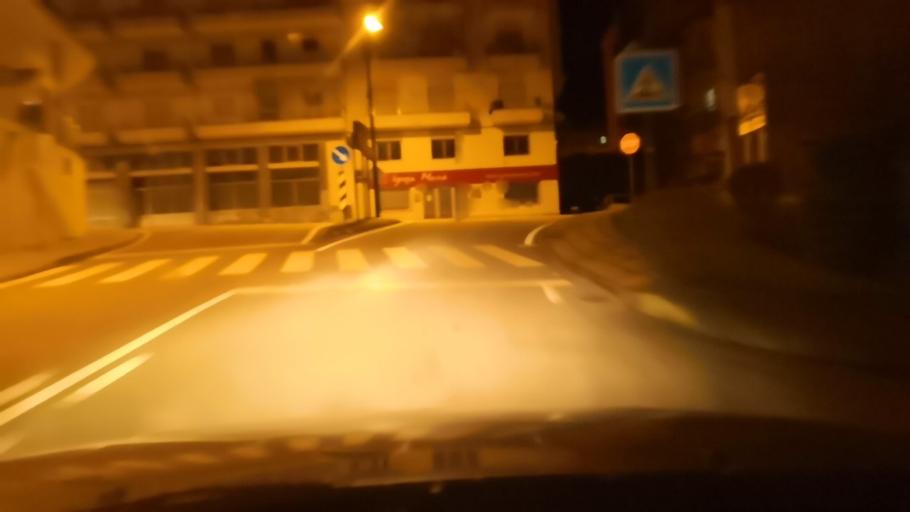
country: PT
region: Castelo Branco
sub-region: Concelho do Fundao
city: Fundao
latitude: 40.1359
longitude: -7.5050
